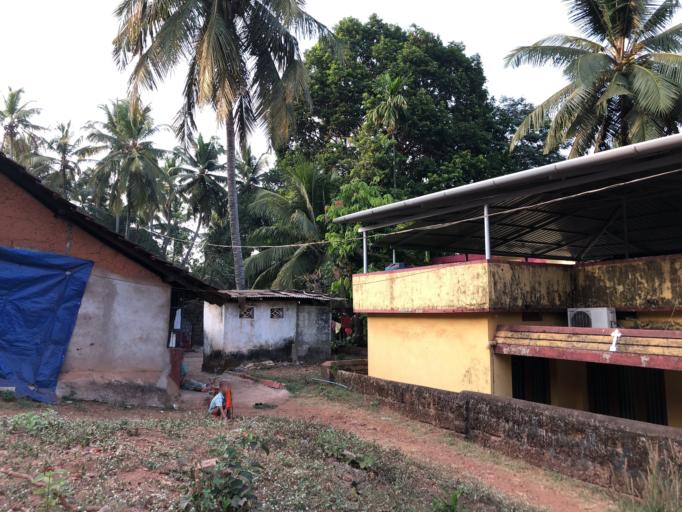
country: IN
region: Karnataka
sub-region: Dakshina Kannada
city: Mangalore
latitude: 12.8873
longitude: 74.8674
